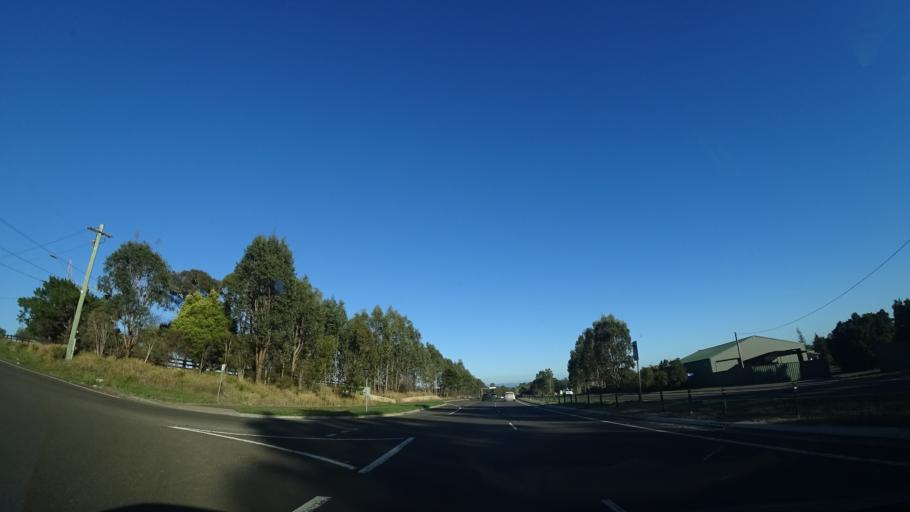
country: AU
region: New South Wales
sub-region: Blacktown
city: Rouse Hill
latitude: -33.6727
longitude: 150.9065
